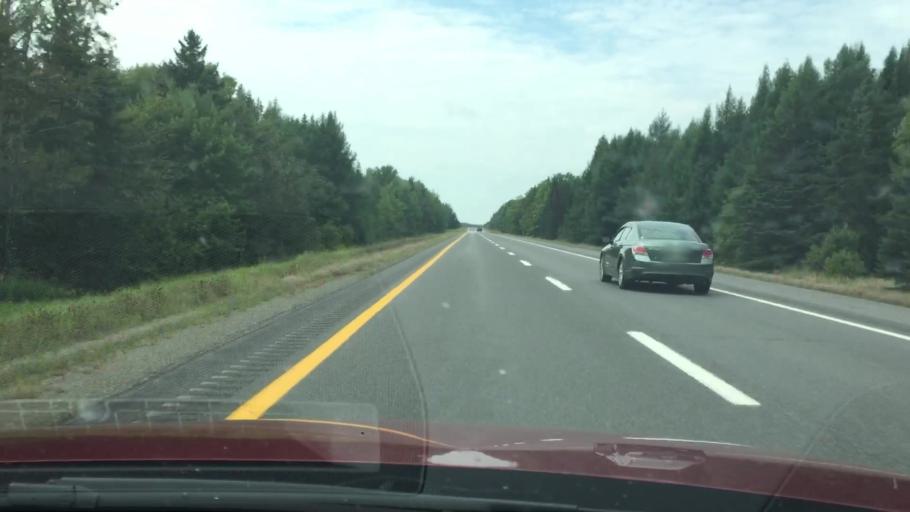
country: US
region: Maine
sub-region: Aroostook County
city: Houlton
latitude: 46.1371
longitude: -67.8800
